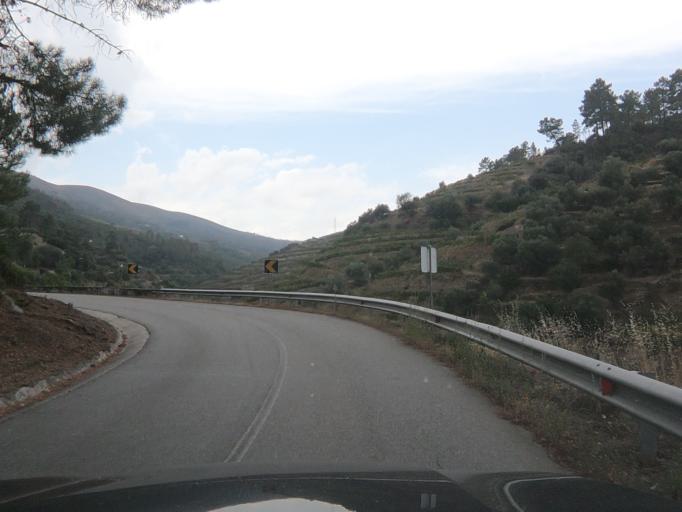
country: PT
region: Vila Real
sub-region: Sabrosa
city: Vilela
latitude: 41.1975
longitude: -7.5485
